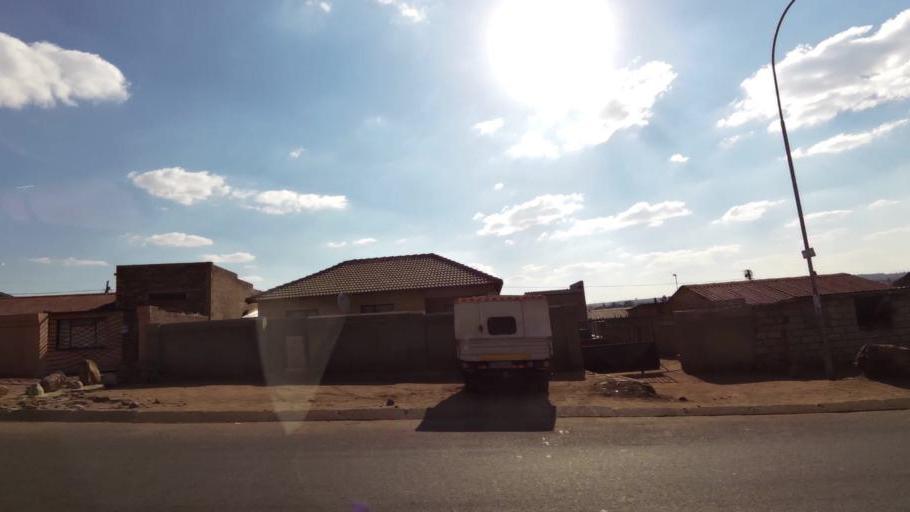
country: ZA
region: Gauteng
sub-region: City of Johannesburg Metropolitan Municipality
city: Soweto
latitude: -26.2262
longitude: 27.8783
